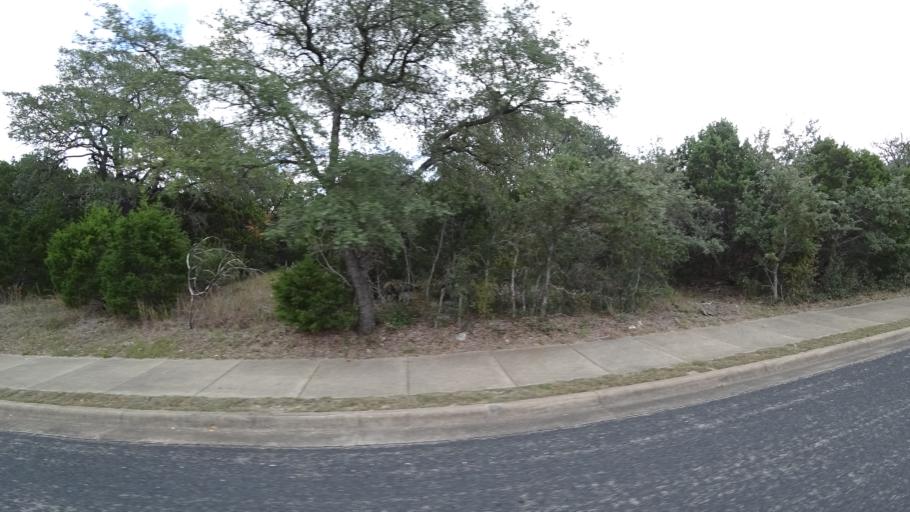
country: US
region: Texas
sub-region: Williamson County
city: Anderson Mill
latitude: 30.4171
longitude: -97.8506
